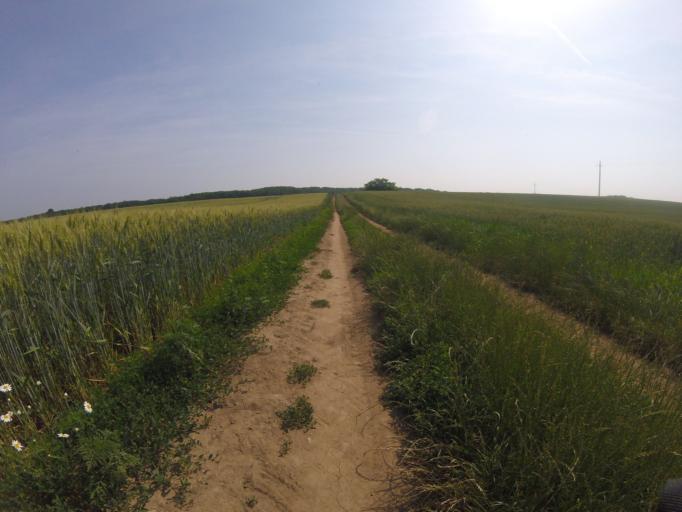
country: HU
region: Tolna
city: Bolcske
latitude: 46.7360
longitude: 18.9384
